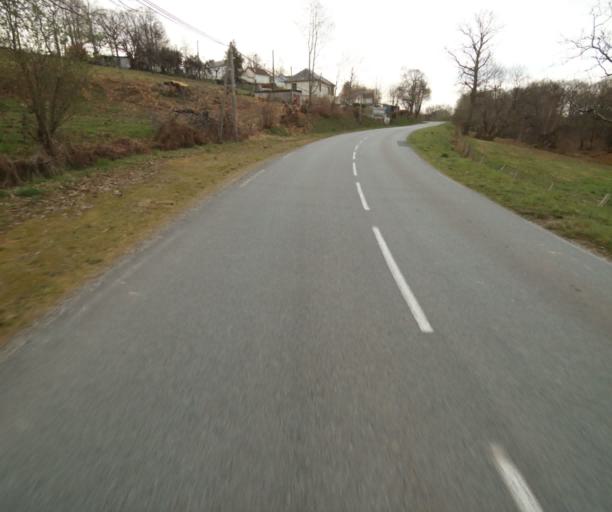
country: FR
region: Limousin
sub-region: Departement de la Correze
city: Correze
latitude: 45.4293
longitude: 1.8309
